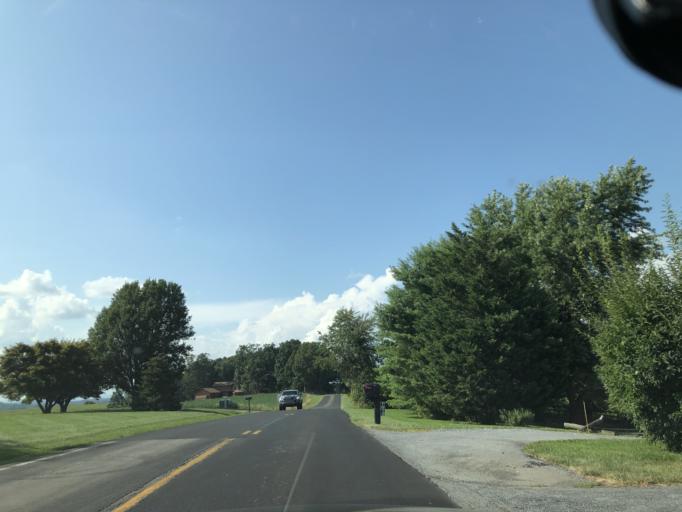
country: US
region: Maryland
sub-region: Frederick County
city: Linganore
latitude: 39.4484
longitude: -77.1768
